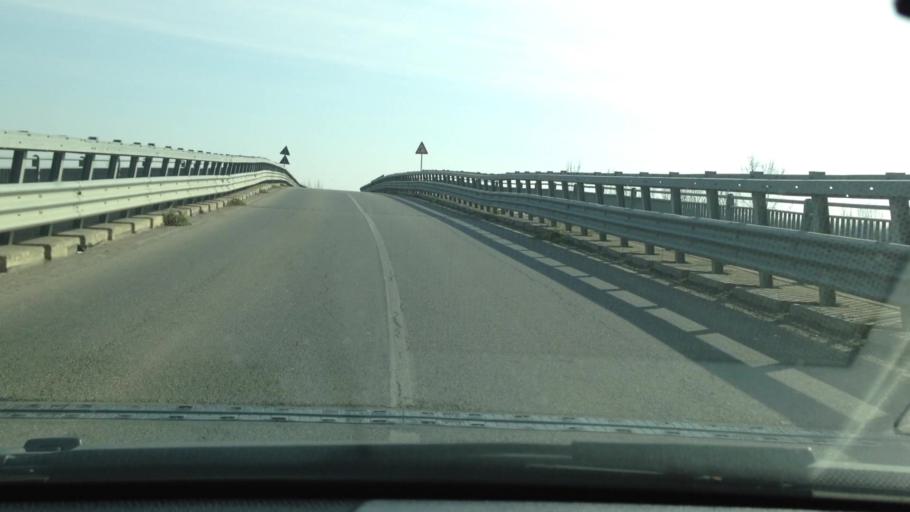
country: IT
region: Piedmont
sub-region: Provincia di Alessandria
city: Felizzano
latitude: 44.8984
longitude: 8.4499
